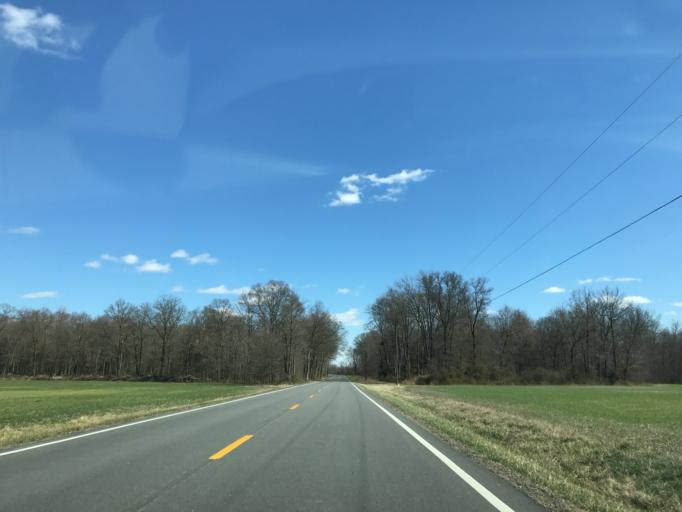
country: US
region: Delaware
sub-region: Kent County
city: Clayton
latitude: 39.2528
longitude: -75.7986
